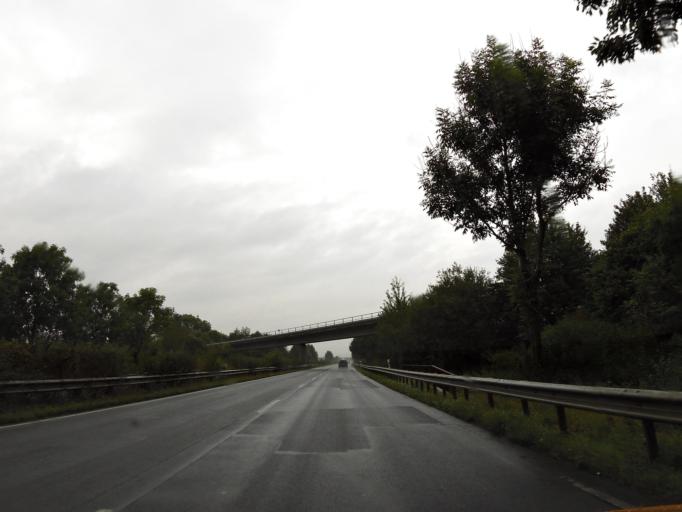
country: DE
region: Lower Saxony
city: Bovenden
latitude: 51.5687
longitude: 9.9203
